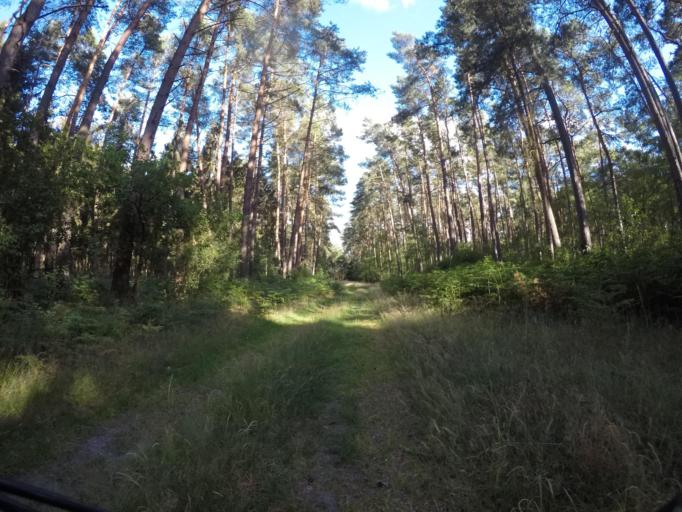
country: DE
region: Mecklenburg-Vorpommern
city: Lubtheen
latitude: 53.2417
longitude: 11.0199
